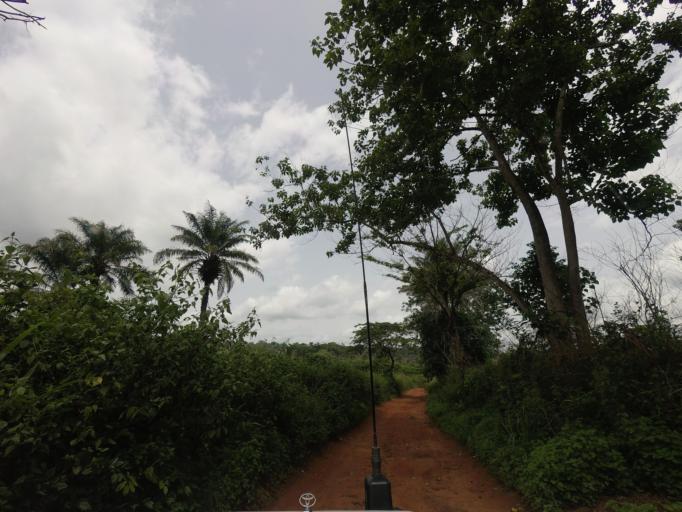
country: GN
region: Nzerekore
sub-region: Prefecture de Guekedou
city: Gueckedou
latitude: 8.4913
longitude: -10.3323
